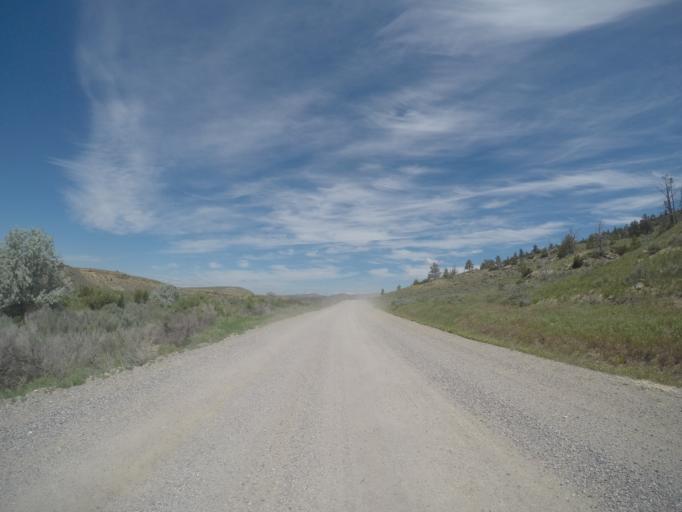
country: US
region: Montana
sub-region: Carbon County
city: Red Lodge
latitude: 45.2153
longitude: -108.8421
